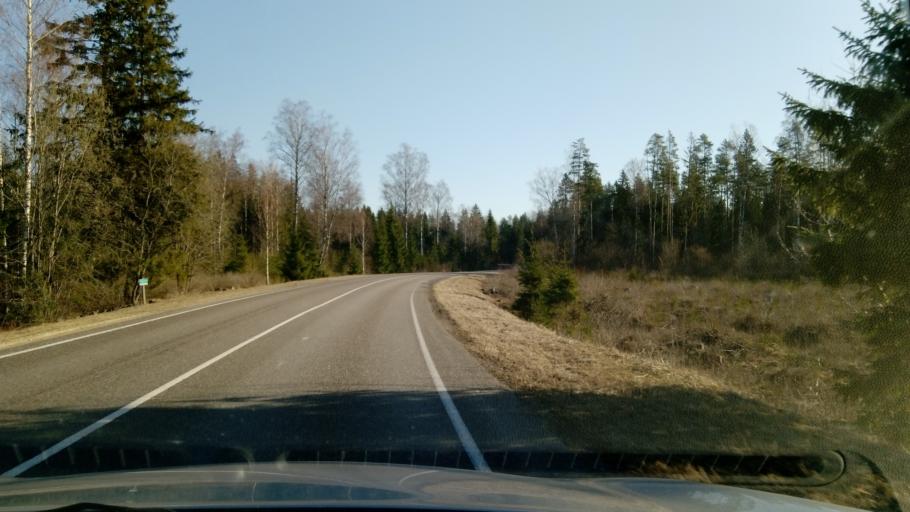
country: EE
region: Jaervamaa
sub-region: Jaerva-Jaani vald
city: Jarva-Jaani
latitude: 59.0517
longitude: 25.9122
